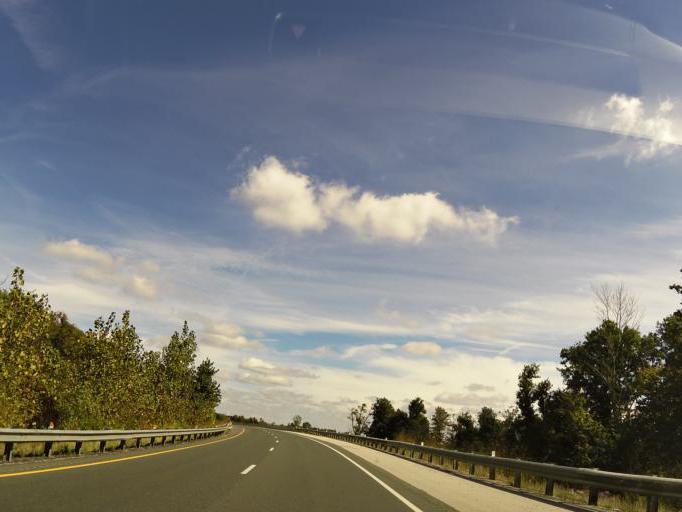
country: CA
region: Ontario
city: London
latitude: 42.9038
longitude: -81.2362
